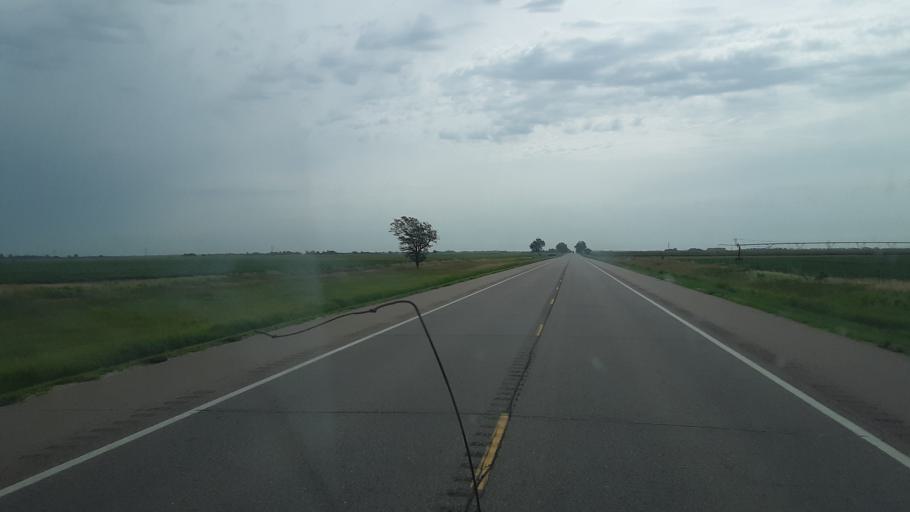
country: US
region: Kansas
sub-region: Stafford County
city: Saint John
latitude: 37.9560
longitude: -98.8007
